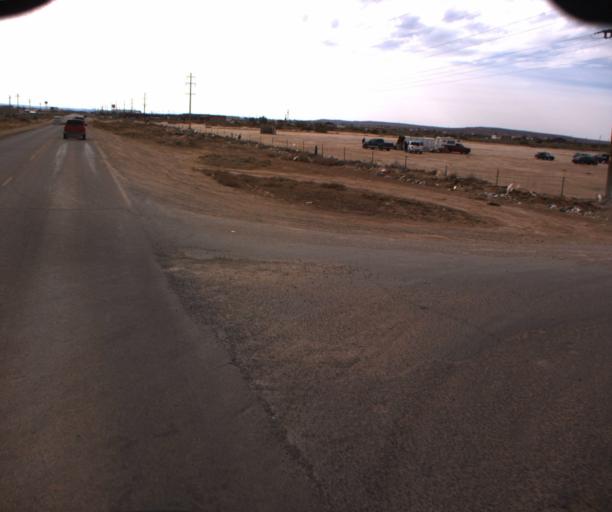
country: US
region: Arizona
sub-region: Apache County
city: Chinle
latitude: 36.1703
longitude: -109.5868
